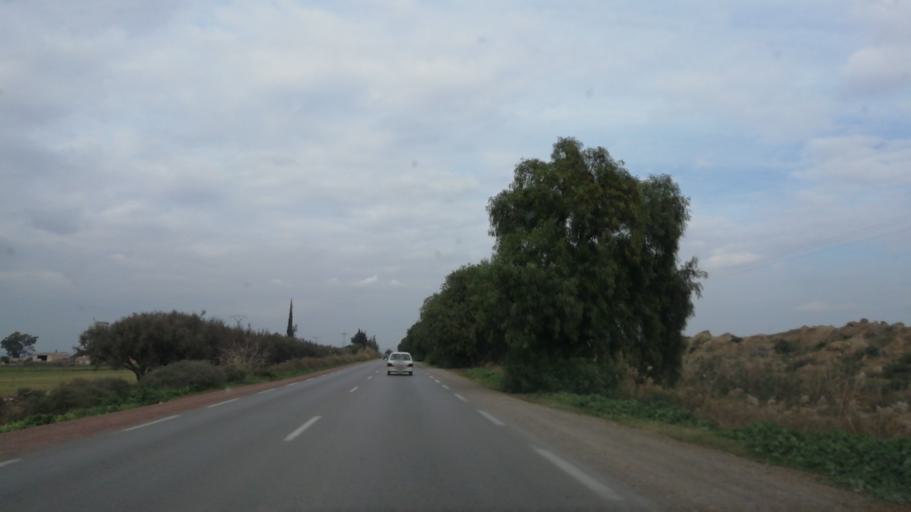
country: DZ
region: Mostaganem
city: Mostaganem
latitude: 35.6596
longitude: 0.0587
